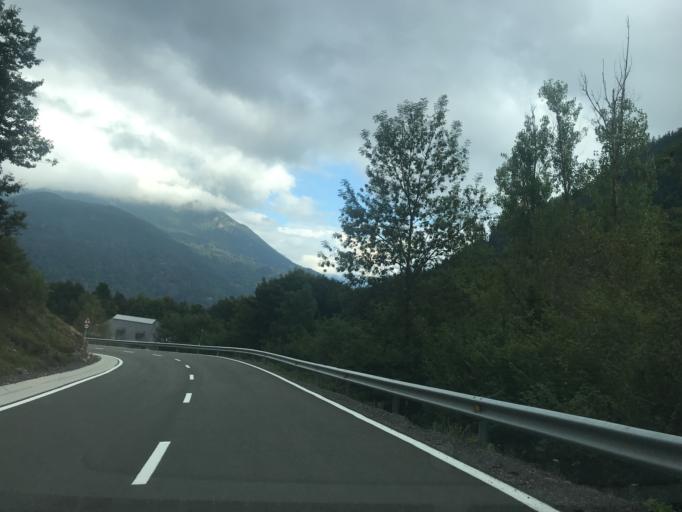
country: ES
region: Catalonia
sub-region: Provincia de Lleida
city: Les
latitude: 42.7681
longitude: 0.6693
